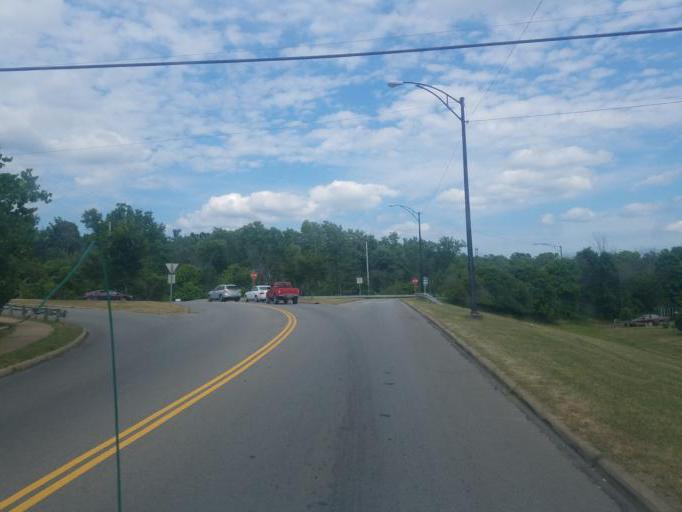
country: US
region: Ohio
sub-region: Guernsey County
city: Cambridge
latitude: 40.0199
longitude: -81.5887
